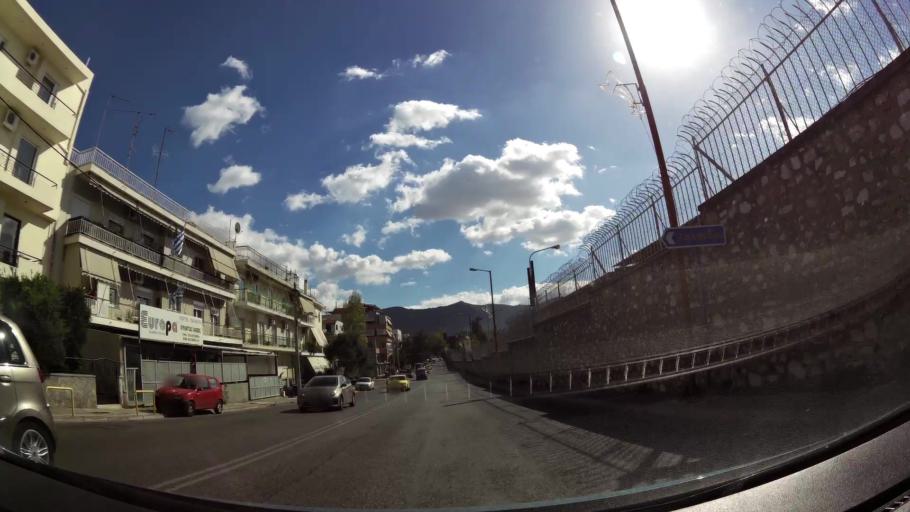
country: GR
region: Attica
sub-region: Nomarchia Athinas
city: Neo Psychiko
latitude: 38.0031
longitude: 23.7829
